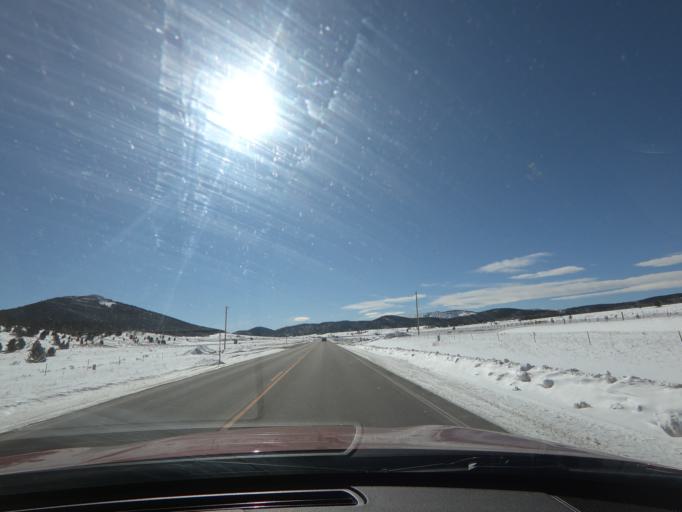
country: US
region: Colorado
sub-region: Teller County
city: Cripple Creek
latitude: 38.7892
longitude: -105.1243
